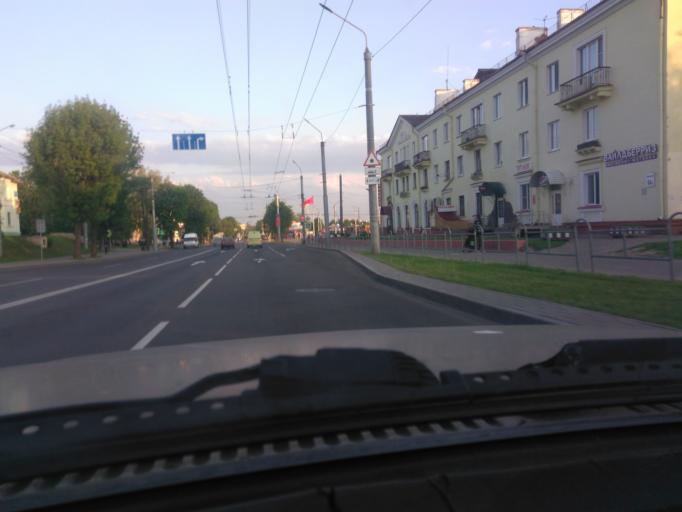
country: BY
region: Mogilev
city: Mahilyow
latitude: 53.9278
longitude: 30.3391
